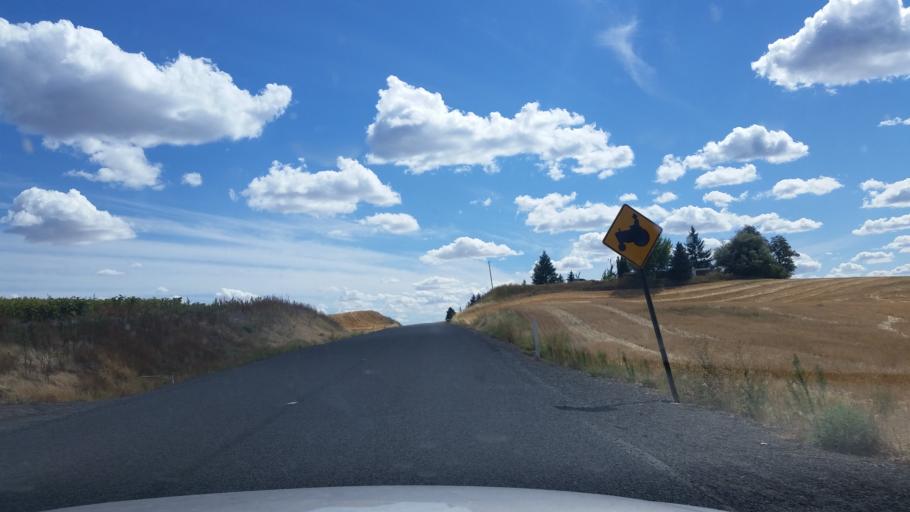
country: US
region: Washington
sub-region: Spokane County
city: Cheney
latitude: 47.4869
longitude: -117.6164
